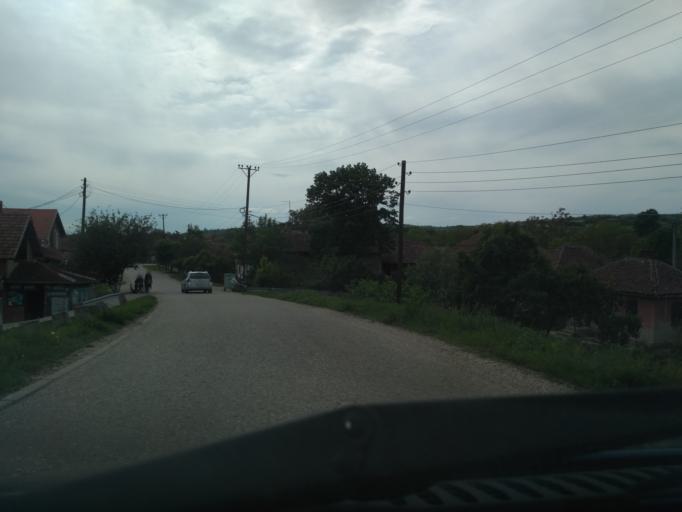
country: RS
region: Central Serbia
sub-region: Podunavski Okrug
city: Velika Plana
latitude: 44.3693
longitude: 21.0768
